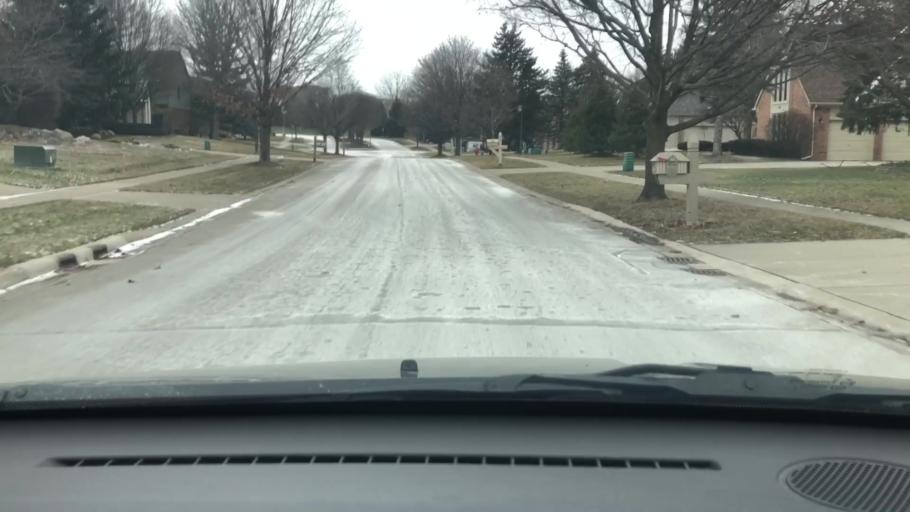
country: US
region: Michigan
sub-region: Oakland County
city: Rochester
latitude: 42.6925
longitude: -83.1154
